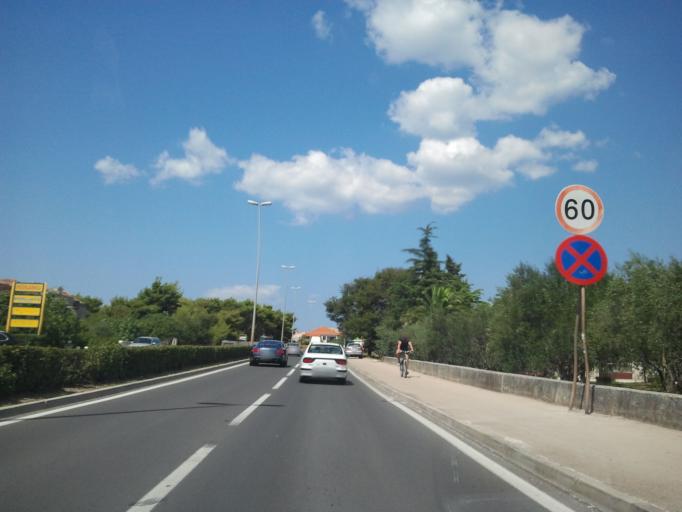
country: HR
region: Zadarska
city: Zadar
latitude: 44.1108
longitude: 15.2572
